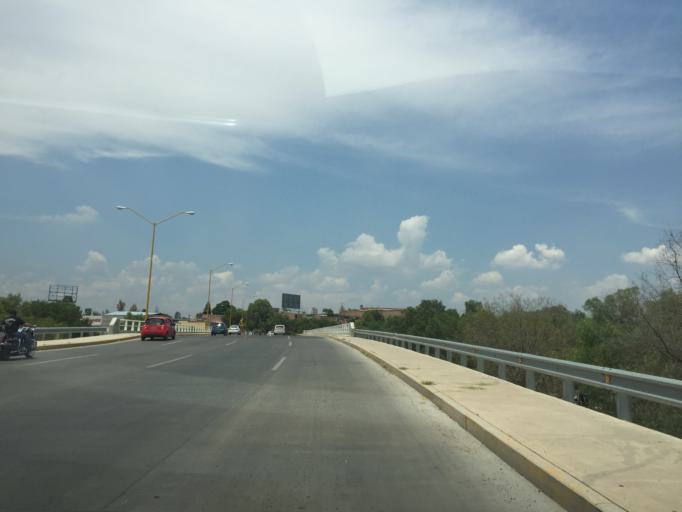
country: MX
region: Aguascalientes
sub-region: Aguascalientes
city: La Loma de los Negritos
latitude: 21.8643
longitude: -102.3208
